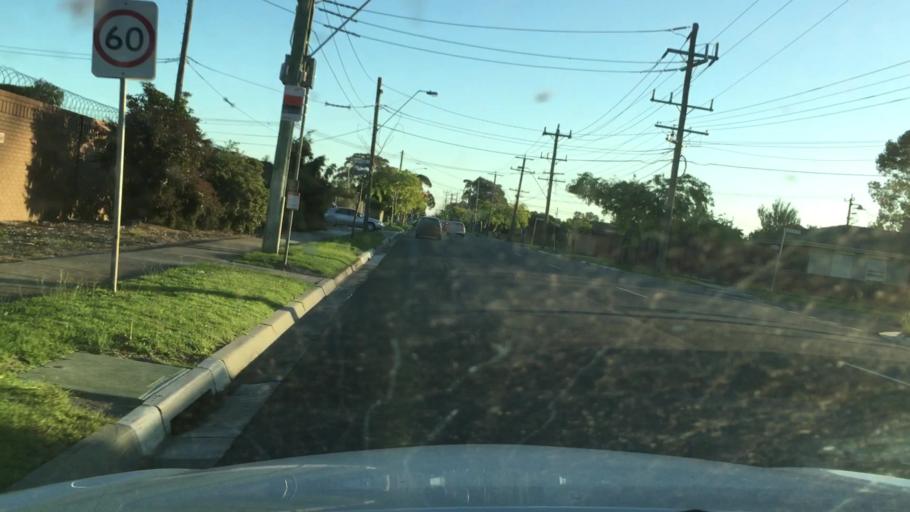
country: AU
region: Victoria
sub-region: Greater Dandenong
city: Noble Park
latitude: -37.9783
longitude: 145.1659
